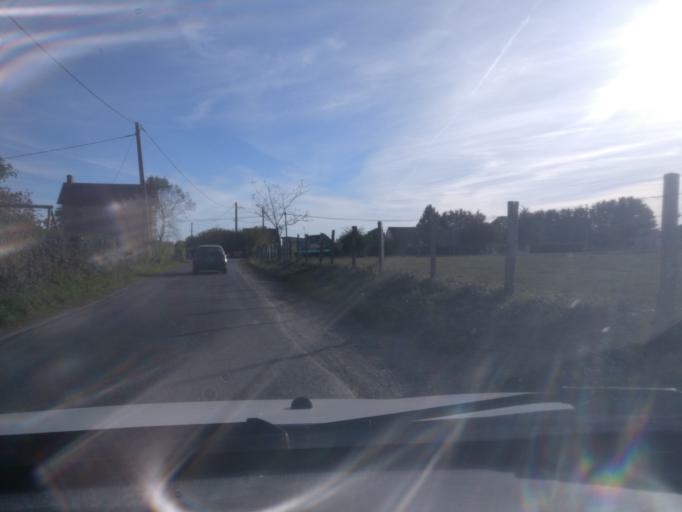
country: FR
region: Lower Normandy
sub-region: Departement de la Manche
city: Sartilly
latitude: 48.7108
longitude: -1.4862
